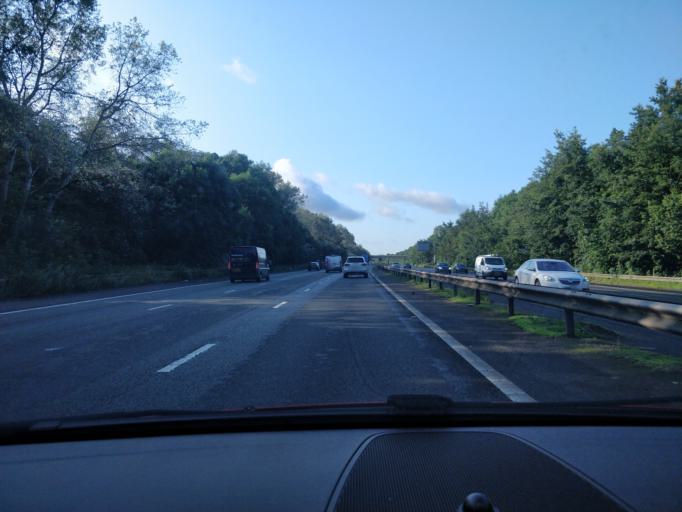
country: GB
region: England
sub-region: Knowsley
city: Knowsley
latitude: 53.4450
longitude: -2.8596
